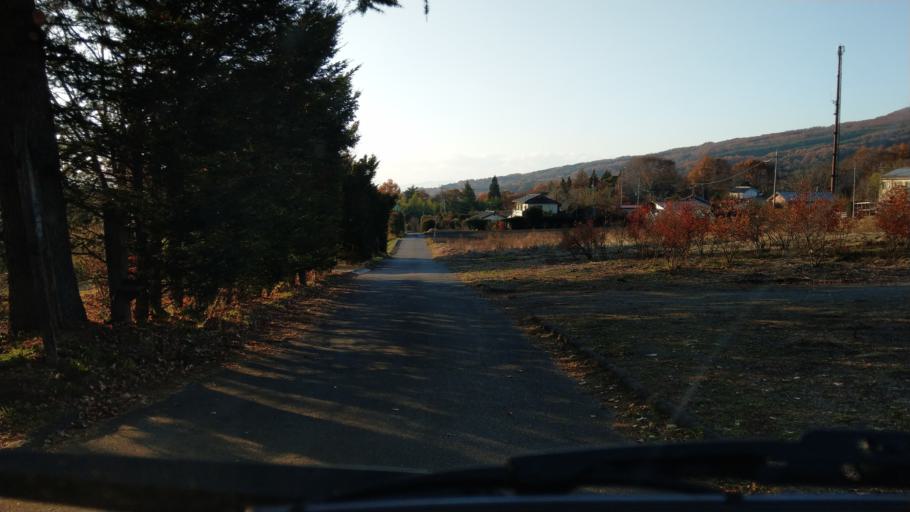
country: JP
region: Nagano
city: Komoro
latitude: 36.3523
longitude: 138.4501
